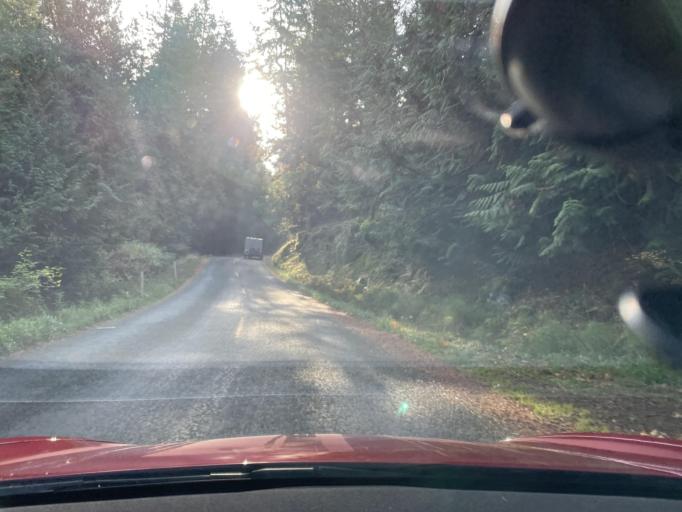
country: US
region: Washington
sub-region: San Juan County
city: Friday Harbor
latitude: 48.5273
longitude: -123.1487
